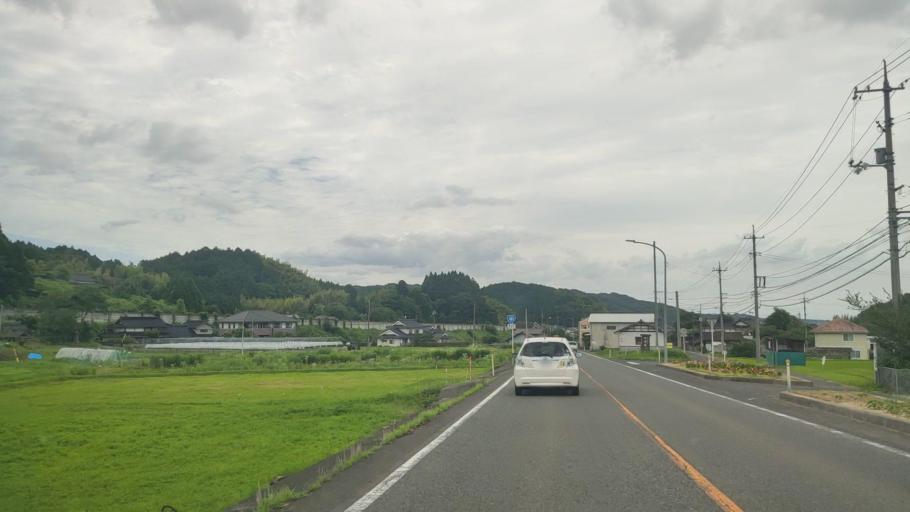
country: JP
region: Okayama
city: Tsuyama
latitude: 35.0597
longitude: 133.8627
